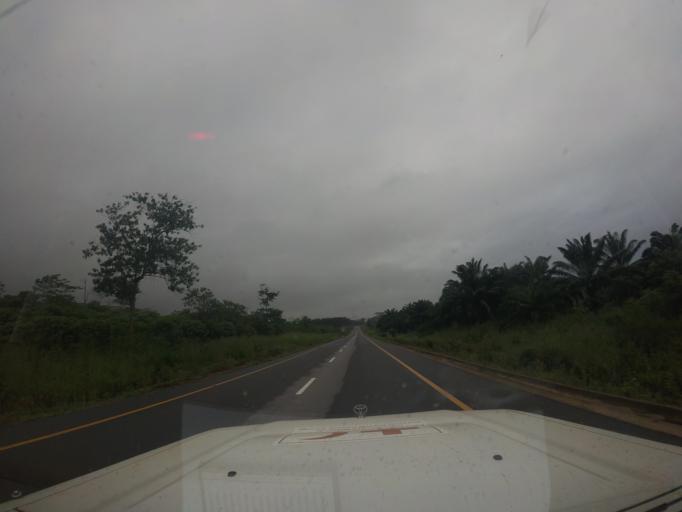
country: SL
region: Eastern Province
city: Hangha
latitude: 7.9622
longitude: -11.1353
